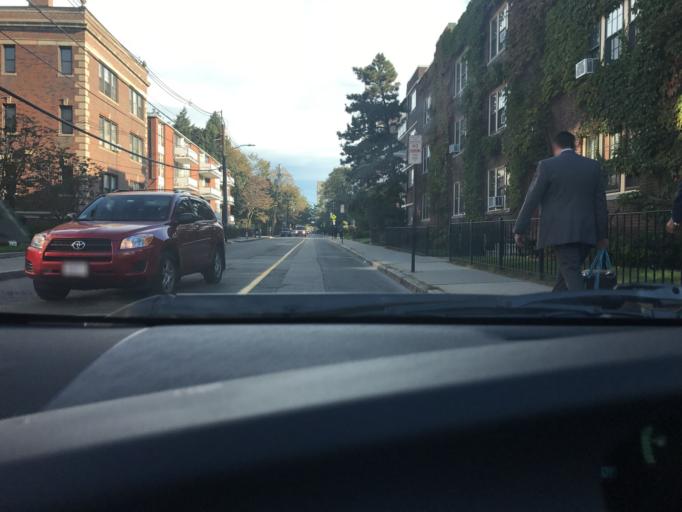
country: US
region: Massachusetts
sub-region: Norfolk County
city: Brookline
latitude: 42.3373
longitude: -71.1251
